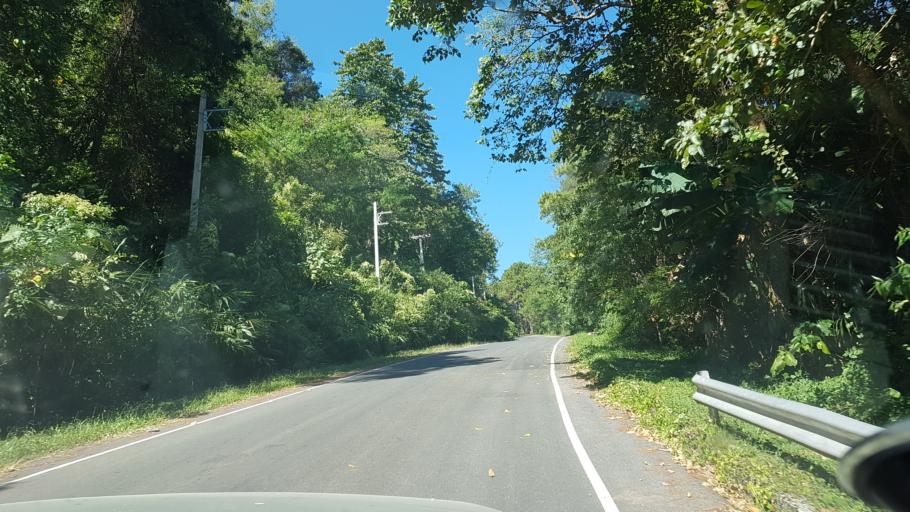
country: TH
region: Phetchabun
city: Khao Kho
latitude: 16.5531
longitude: 100.9775
